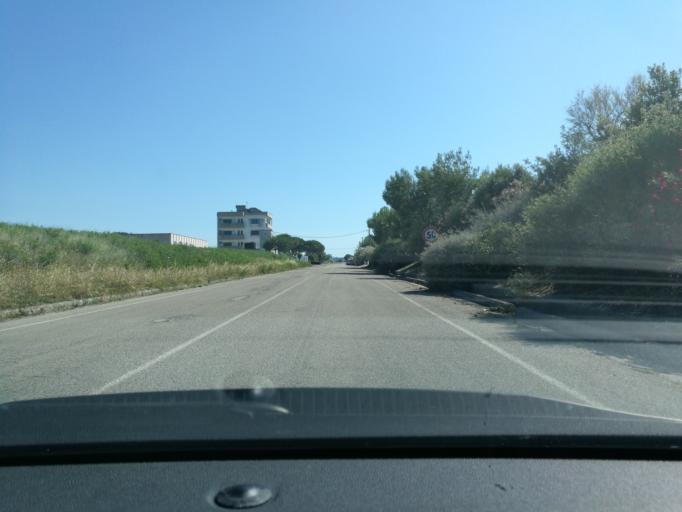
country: IT
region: Abruzzo
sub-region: Provincia di Chieti
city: Vasto
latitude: 42.1736
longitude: 14.6980
